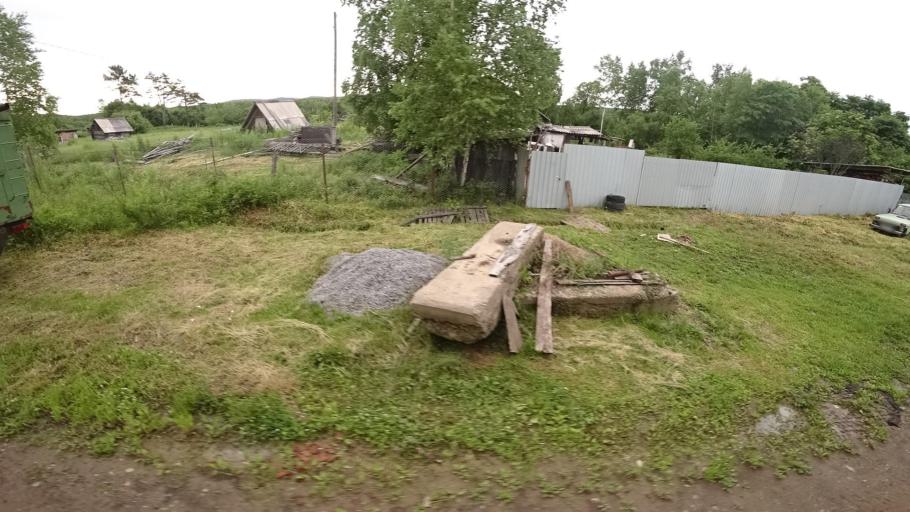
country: RU
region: Khabarovsk Krai
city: Amursk
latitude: 49.9162
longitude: 136.1624
